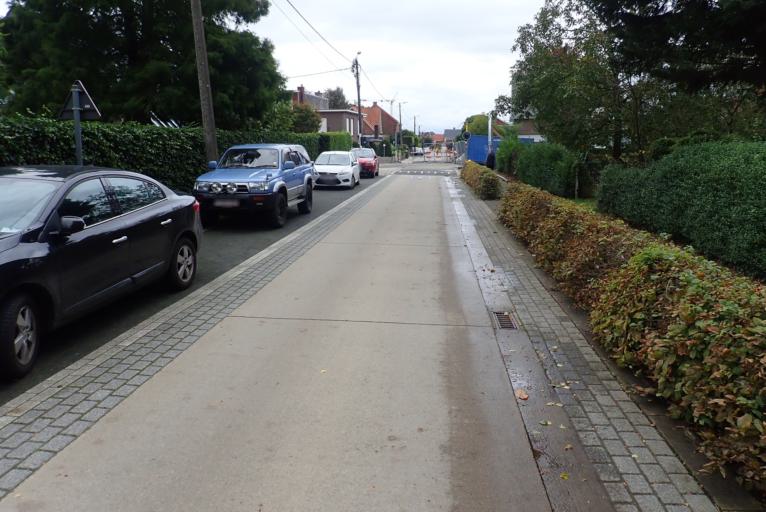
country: BE
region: Flanders
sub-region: Provincie Antwerpen
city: Berlaar
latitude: 51.0845
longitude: 4.6691
